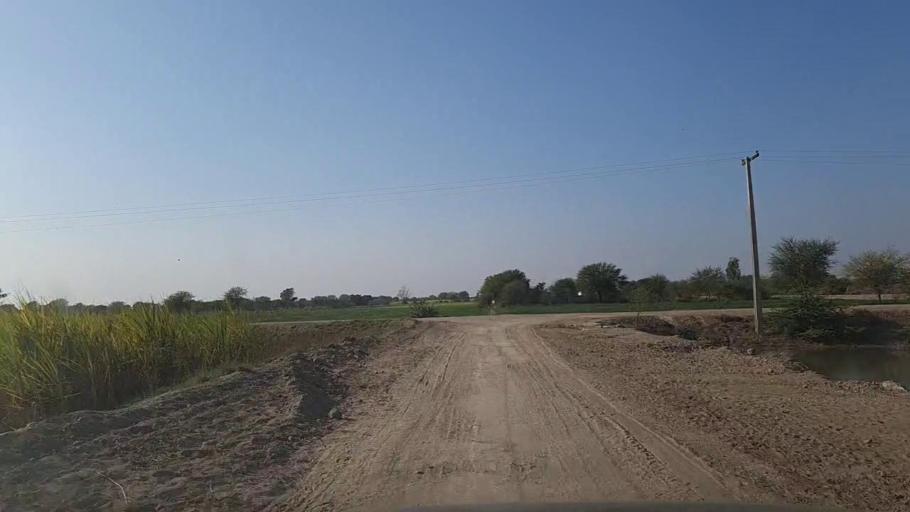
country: PK
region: Sindh
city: Digri
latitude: 25.0229
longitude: 69.2289
